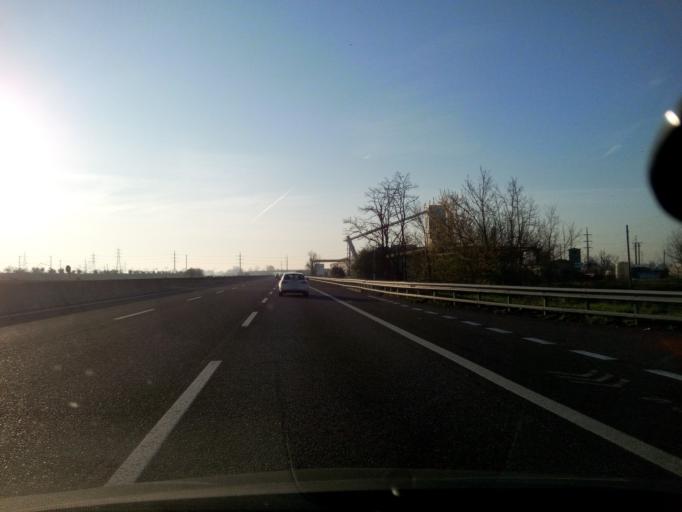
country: IT
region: Lombardy
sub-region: Provincia di Lodi
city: Somaglia
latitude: 45.1326
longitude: 9.6525
